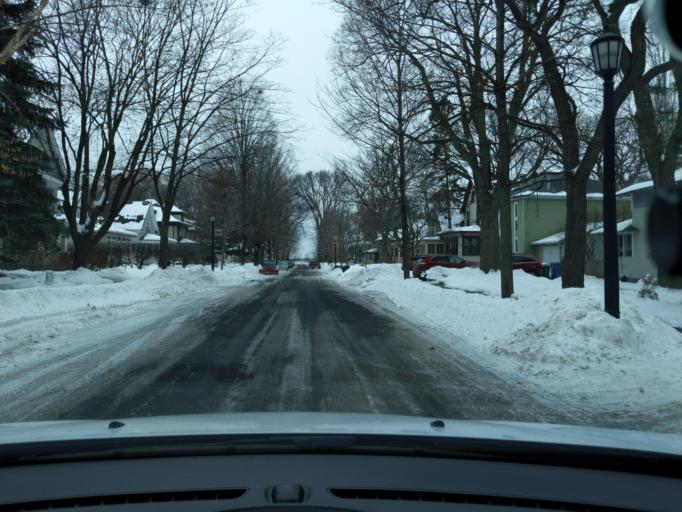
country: US
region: Minnesota
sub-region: Ramsey County
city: Lauderdale
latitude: 44.9625
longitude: -93.2090
